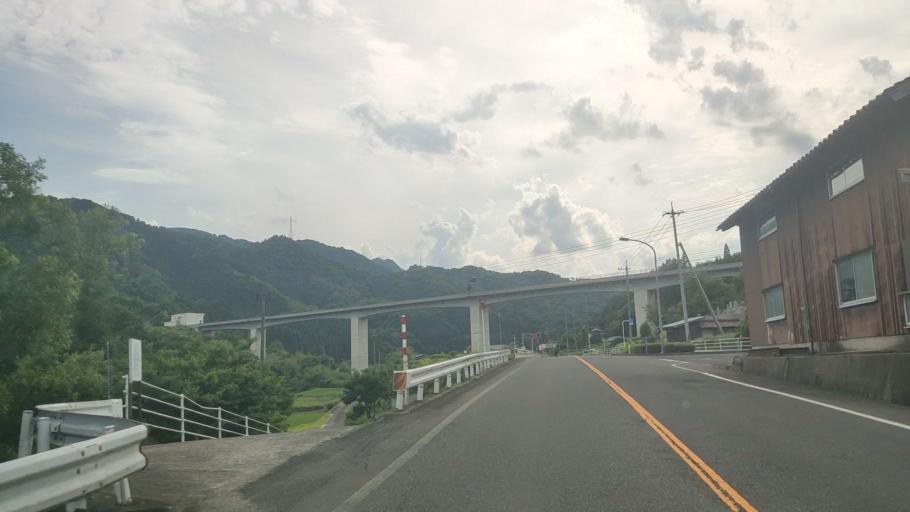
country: JP
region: Tottori
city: Tottori
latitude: 35.3391
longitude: 134.1904
